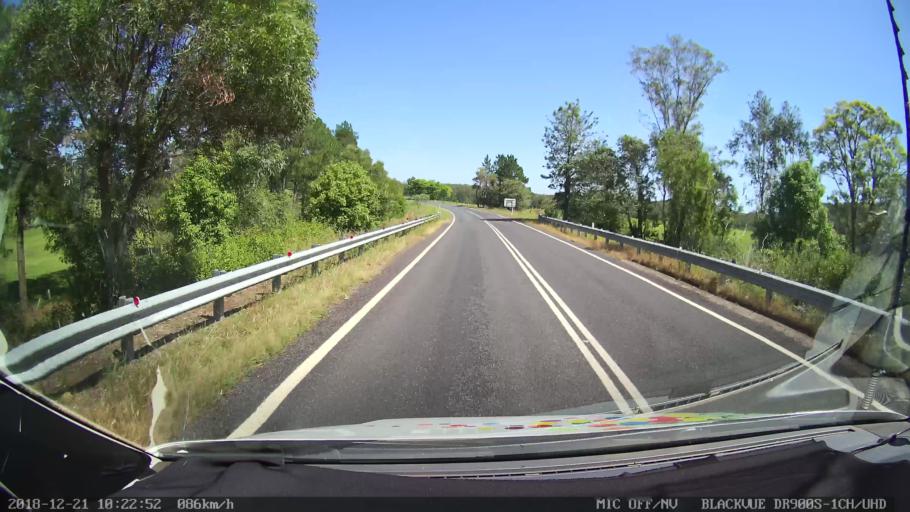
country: AU
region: New South Wales
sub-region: Clarence Valley
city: South Grafton
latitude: -29.6490
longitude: 152.7983
